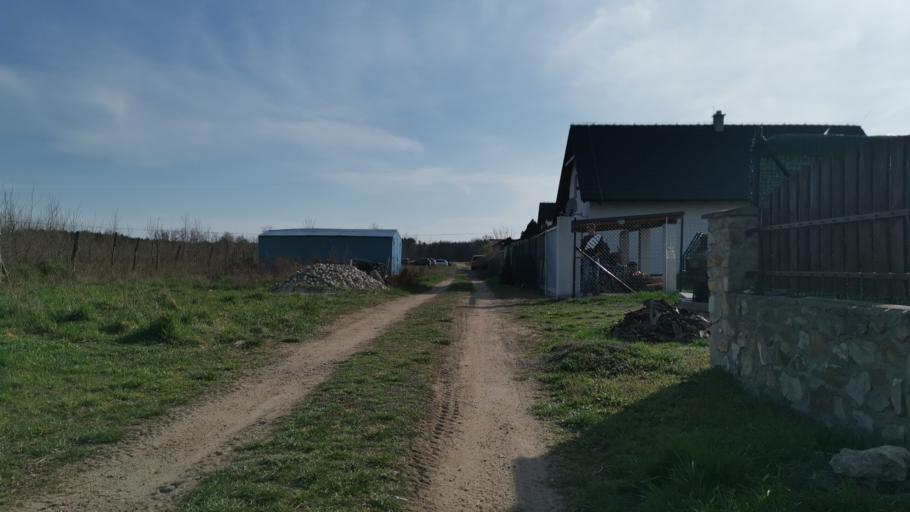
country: CZ
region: South Moravian
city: Tvrdonice
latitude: 48.7272
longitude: 17.0392
